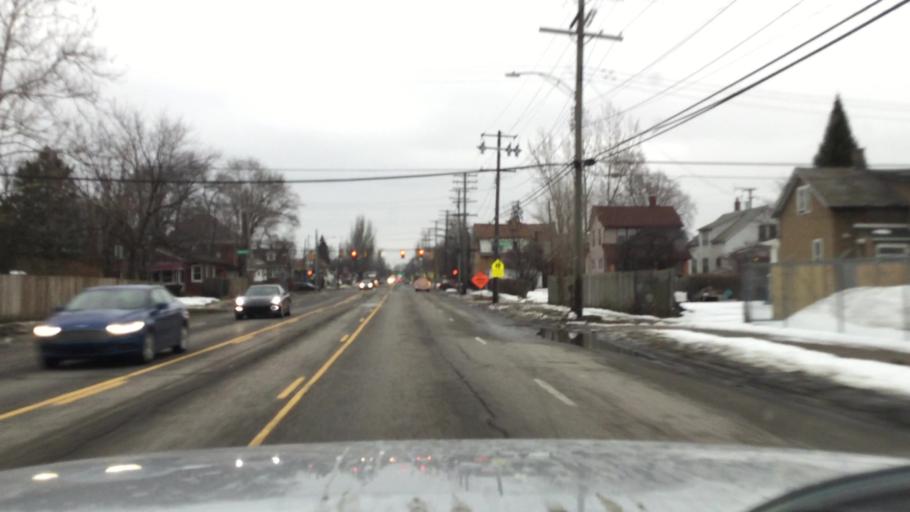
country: US
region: Michigan
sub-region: Wayne County
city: Dearborn
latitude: 42.3326
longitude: -83.1480
